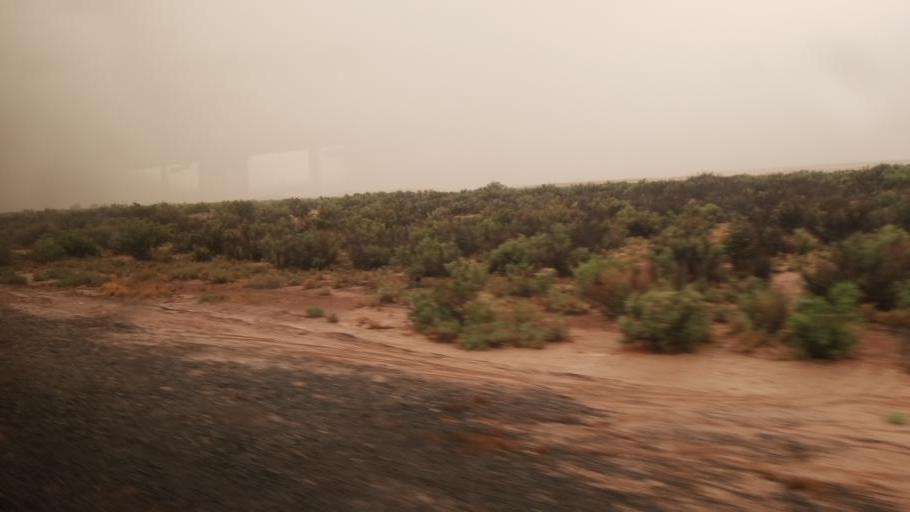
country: US
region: Arizona
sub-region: Navajo County
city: Joseph City
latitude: 34.9547
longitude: -110.3580
